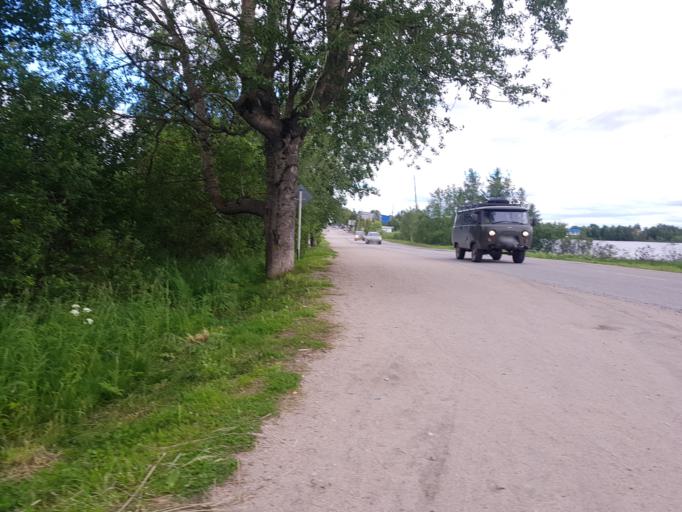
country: RU
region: Republic of Karelia
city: Kalevala
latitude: 65.2007
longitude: 31.1772
